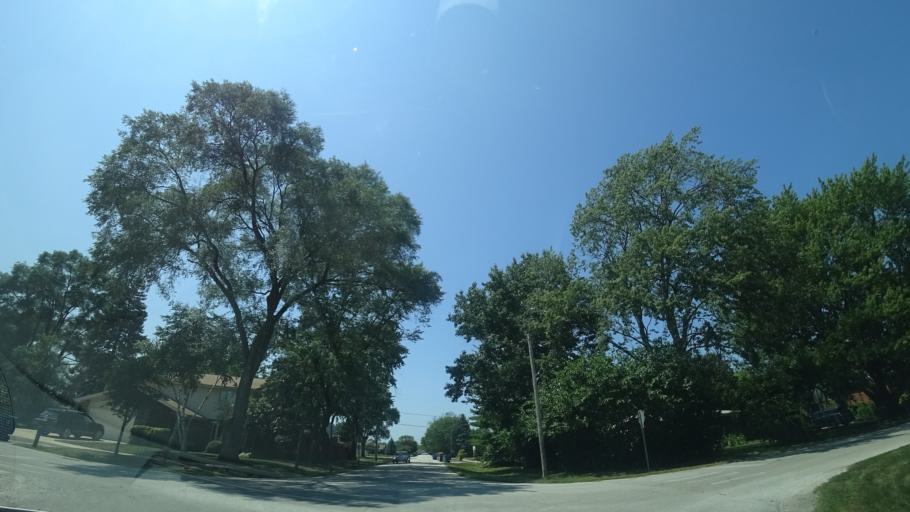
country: US
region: Illinois
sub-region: Cook County
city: Alsip
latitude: 41.6799
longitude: -87.7453
